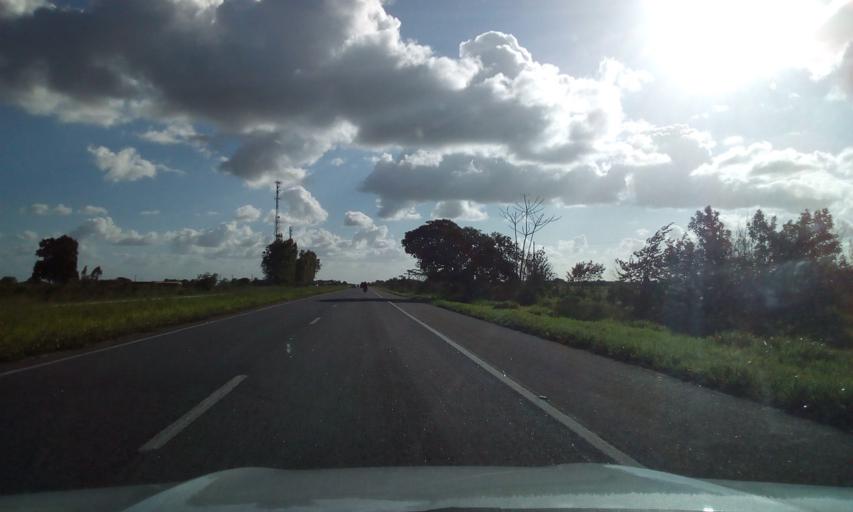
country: BR
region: Paraiba
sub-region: Cruz Do Espirito Santo
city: Cruz do Espirito Santo
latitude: -7.2025
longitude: -35.1090
